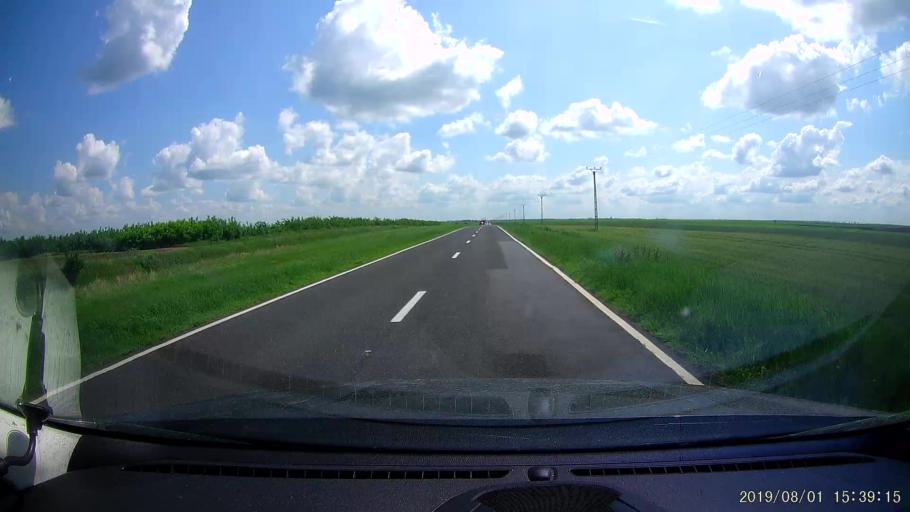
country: RO
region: Braila
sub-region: Comuna Insuratei
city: Insuratei
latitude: 44.8621
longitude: 27.5635
